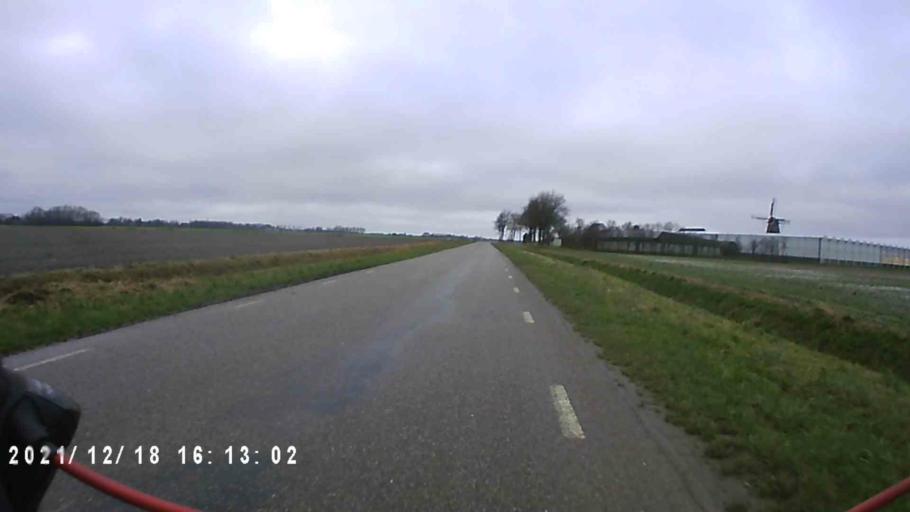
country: NL
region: Friesland
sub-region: Gemeente Dongeradeel
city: Anjum
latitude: 53.3670
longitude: 6.0687
